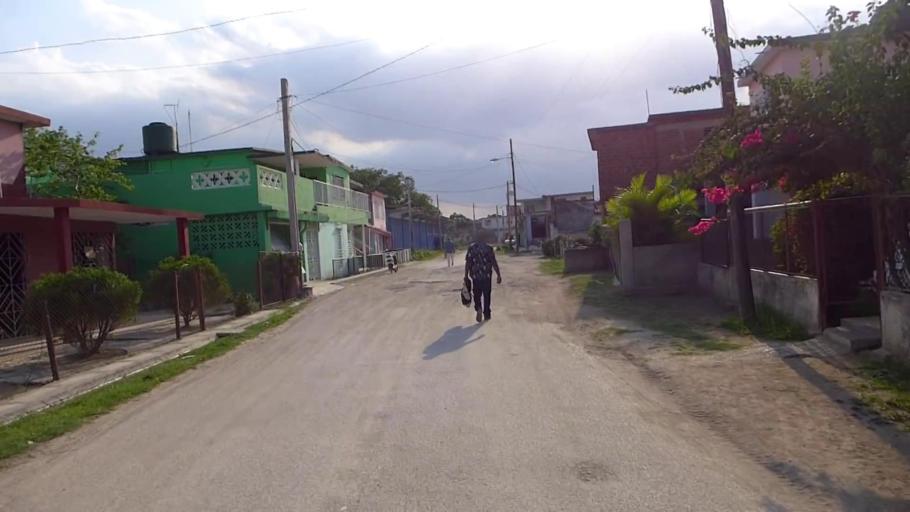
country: CU
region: Camaguey
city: Camaguey
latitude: 21.3883
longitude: -77.9081
